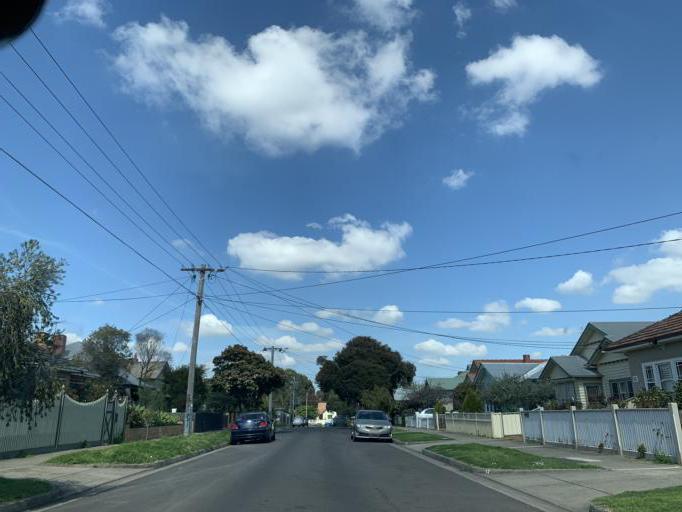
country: AU
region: Victoria
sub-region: Moreland
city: Coburg North
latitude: -37.7354
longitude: 144.9573
